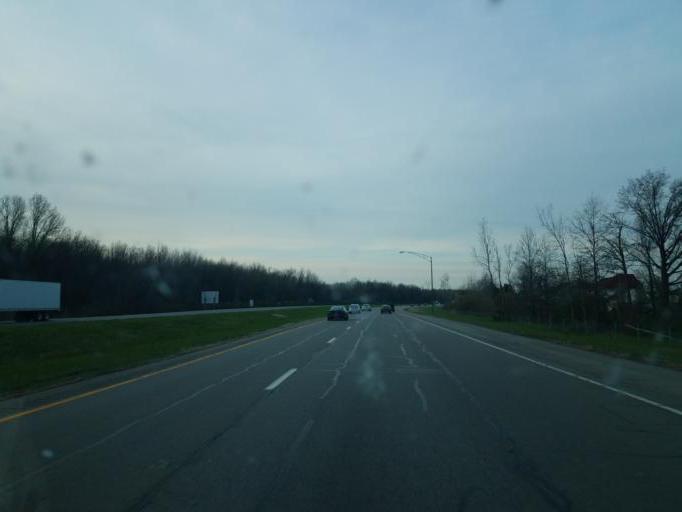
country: US
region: Ohio
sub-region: Lorain County
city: Sheffield
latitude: 41.4291
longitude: -82.0828
